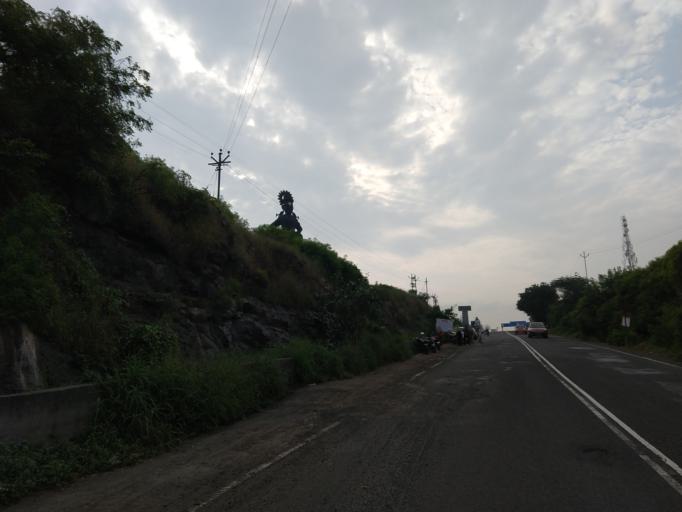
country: IN
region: Maharashtra
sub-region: Pune Division
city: Sasvad
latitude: 18.4156
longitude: 74.0051
